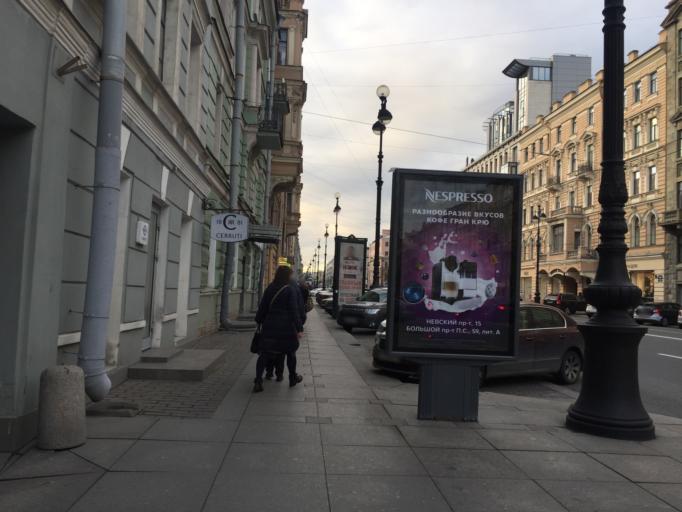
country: RU
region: St.-Petersburg
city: Centralniy
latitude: 59.9272
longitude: 30.3748
